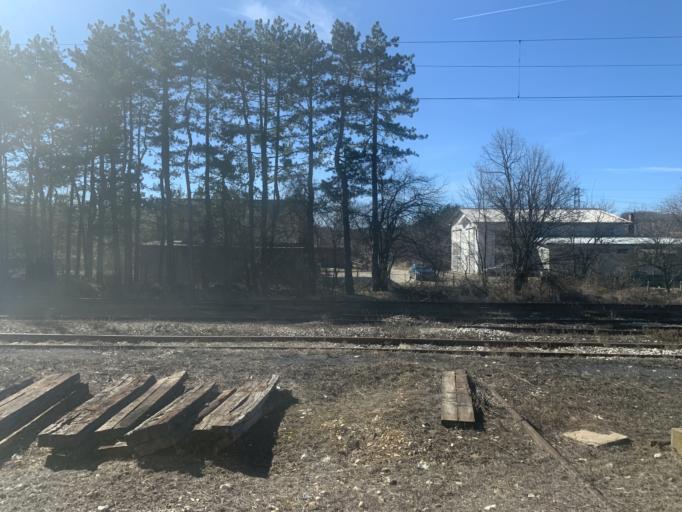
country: BG
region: Sofiya
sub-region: Obshtina Gorna Malina
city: Gorna Malina
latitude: 42.5572
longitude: 23.7056
